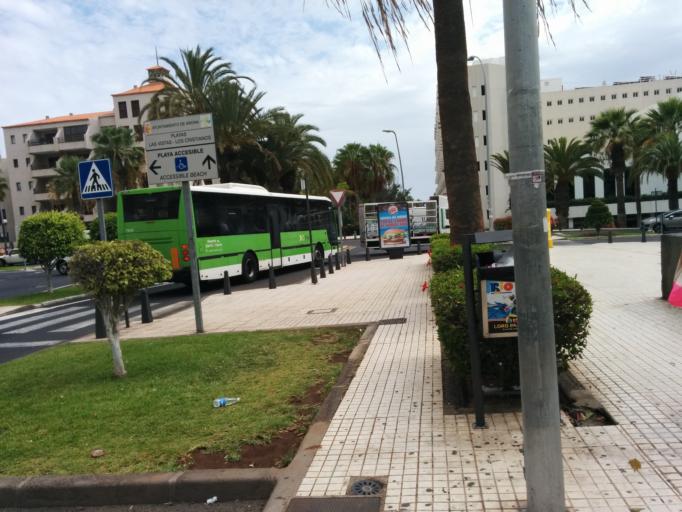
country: ES
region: Canary Islands
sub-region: Provincia de Santa Cruz de Tenerife
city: Playa de las Americas
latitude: 28.0575
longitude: -16.7297
